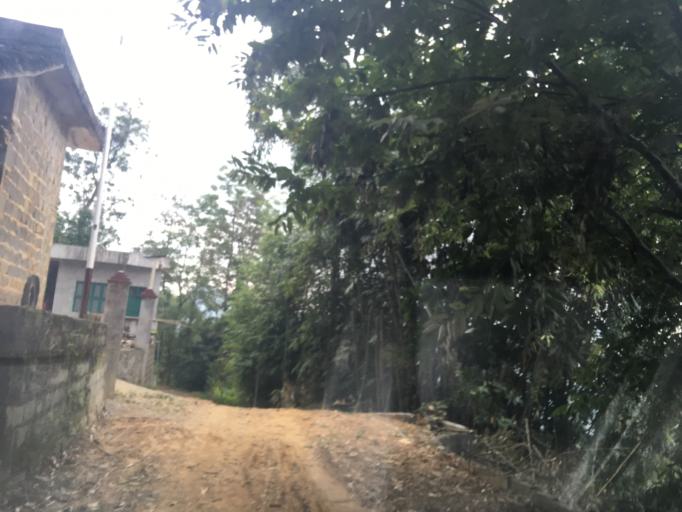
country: CN
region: Guangxi Zhuangzu Zizhiqu
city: Xinzhou
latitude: 25.1663
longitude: 105.6856
